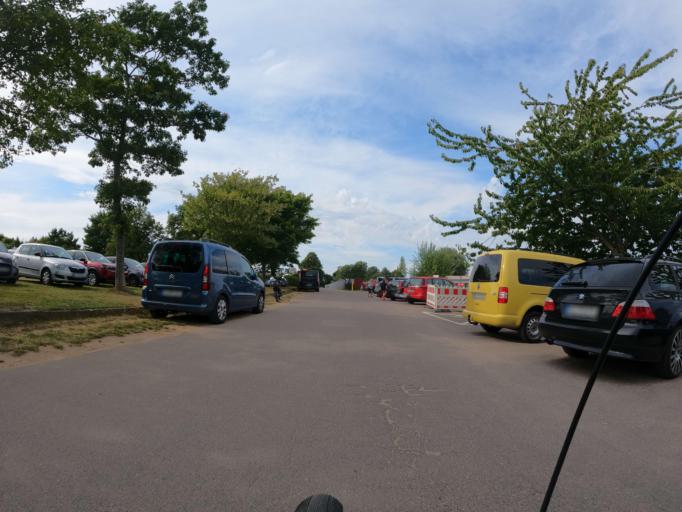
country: DE
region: Schleswig-Holstein
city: Steinberg
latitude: 54.7843
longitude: 9.8004
